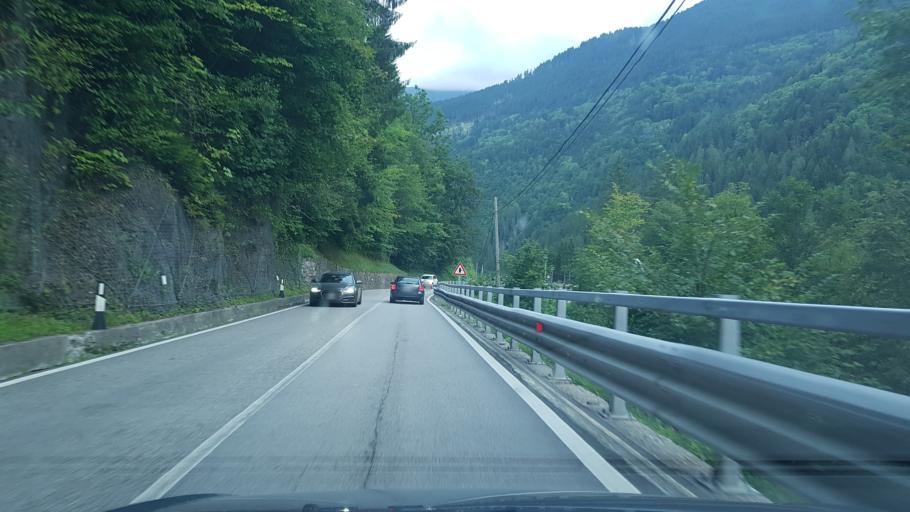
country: IT
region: Friuli Venezia Giulia
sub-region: Provincia di Udine
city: Rigolato
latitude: 46.5567
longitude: 12.8491
